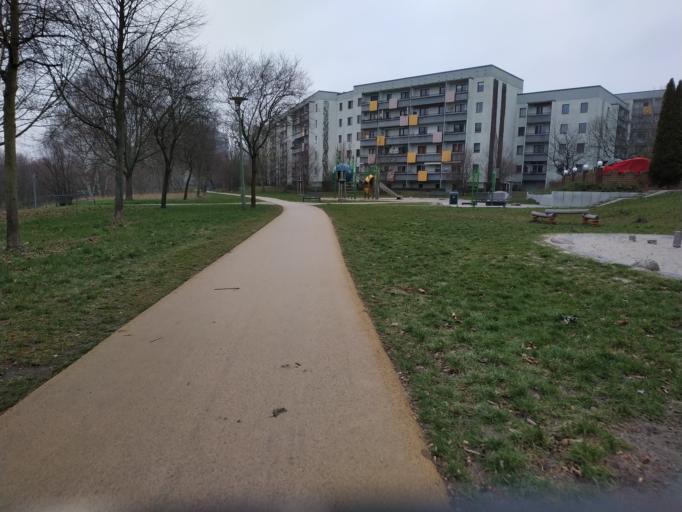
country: DE
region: Berlin
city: Marzahn
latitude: 52.5364
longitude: 13.5869
